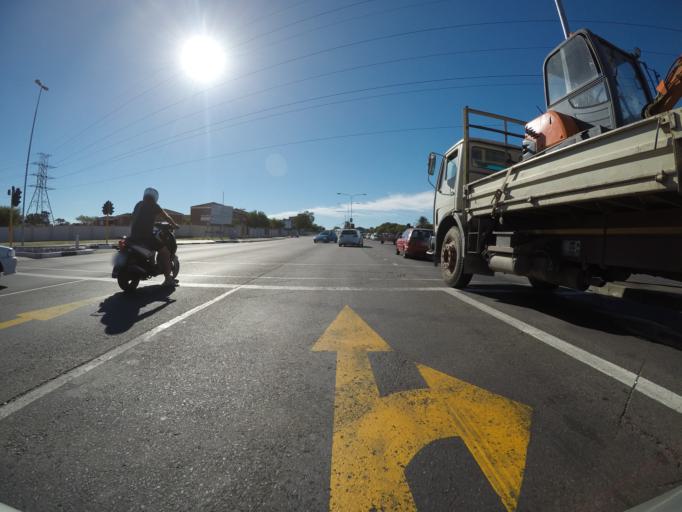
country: ZA
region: Western Cape
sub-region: City of Cape Town
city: Kraaifontein
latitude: -33.9120
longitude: 18.6657
